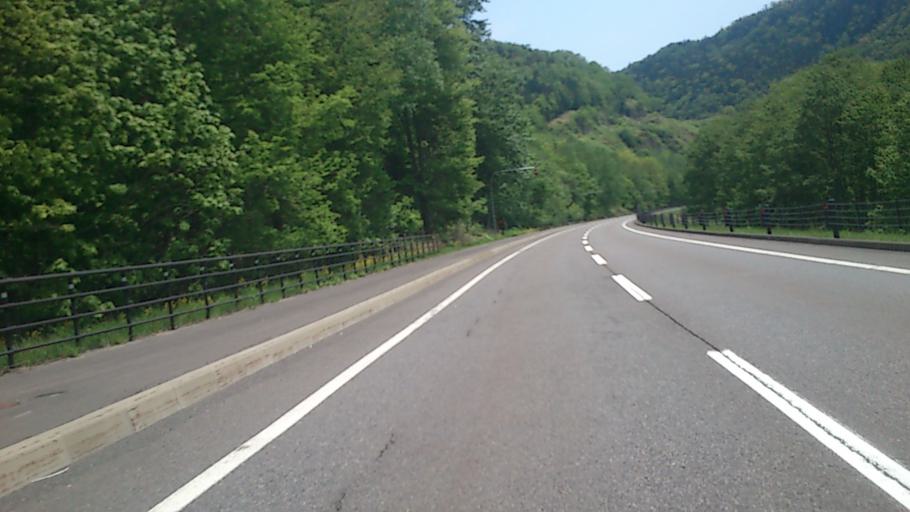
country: JP
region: Hokkaido
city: Otofuke
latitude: 43.3688
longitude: 143.2314
